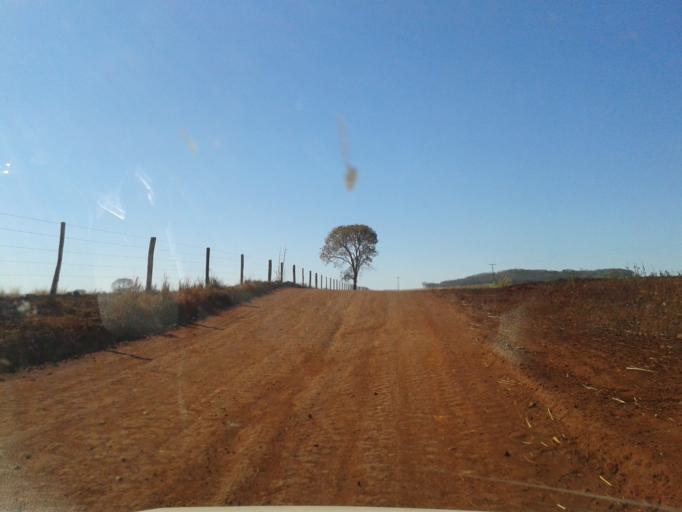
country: BR
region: Minas Gerais
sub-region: Centralina
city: Centralina
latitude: -18.5906
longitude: -49.1747
